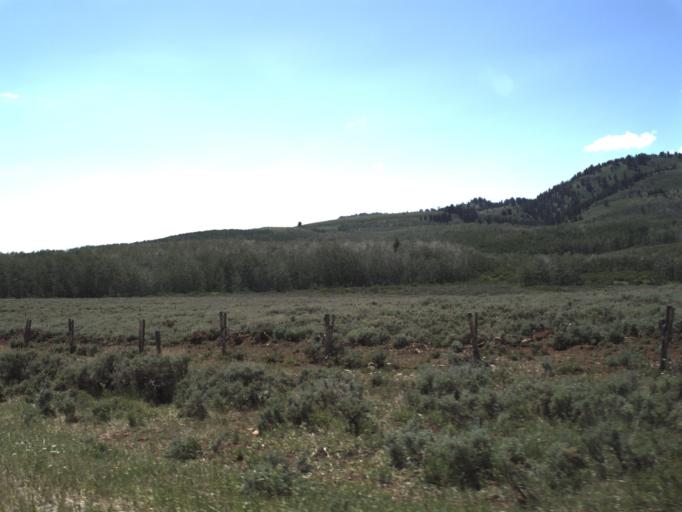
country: US
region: Utah
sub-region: Rich County
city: Randolph
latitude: 41.4796
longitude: -111.4317
